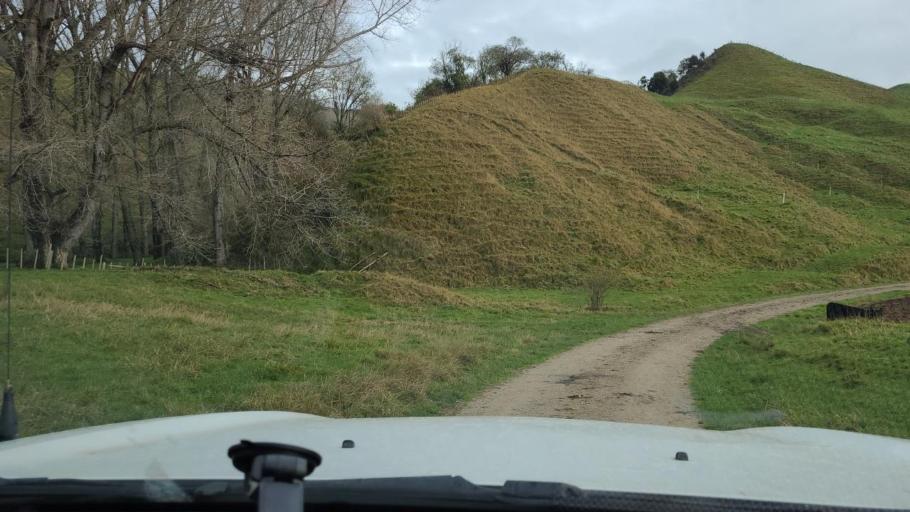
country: NZ
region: Gisborne
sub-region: Gisborne District
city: Gisborne
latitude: -38.5030
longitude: 177.7254
